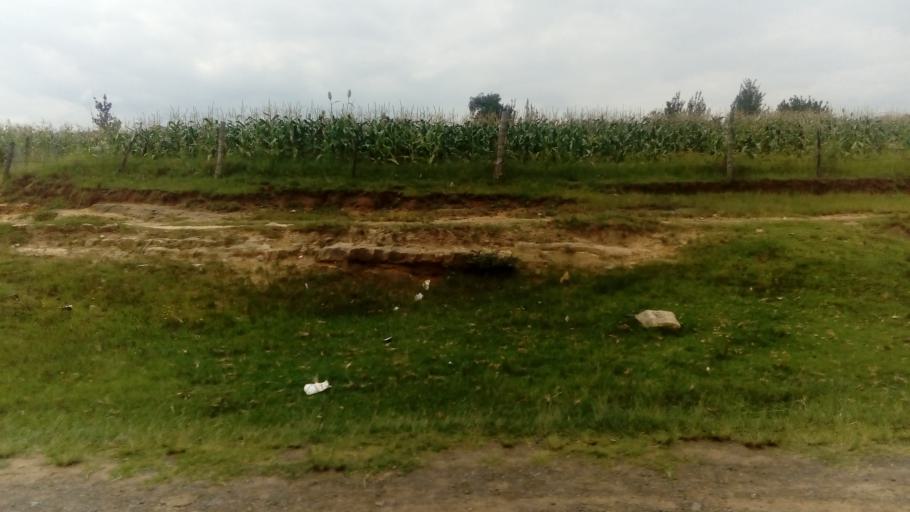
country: LS
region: Leribe
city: Leribe
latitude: -28.9364
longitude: 28.1654
